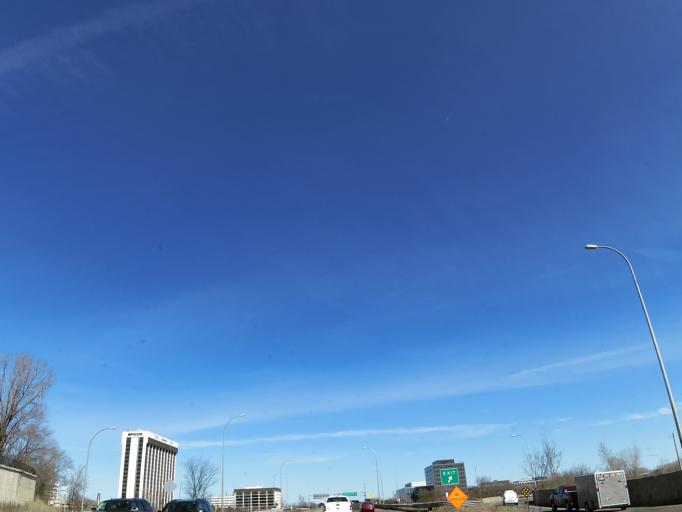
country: US
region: Minnesota
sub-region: Hennepin County
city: Minnetonka Mills
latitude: 44.9704
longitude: -93.4006
